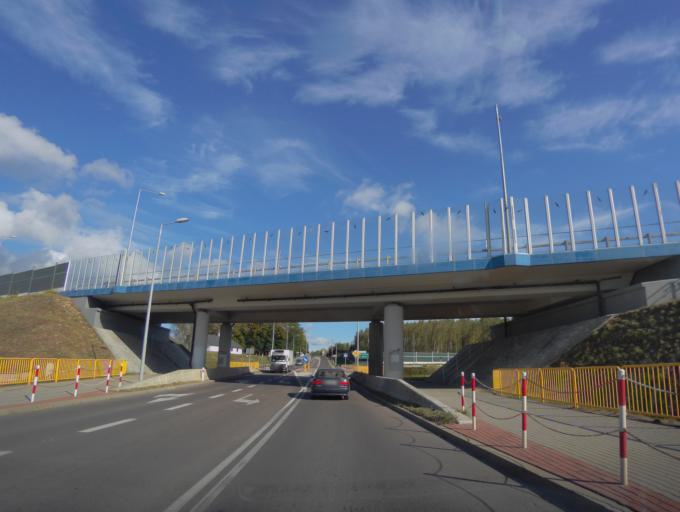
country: PL
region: Subcarpathian Voivodeship
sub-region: Powiat lezajski
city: Giedlarowa
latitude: 50.2405
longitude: 22.4137
